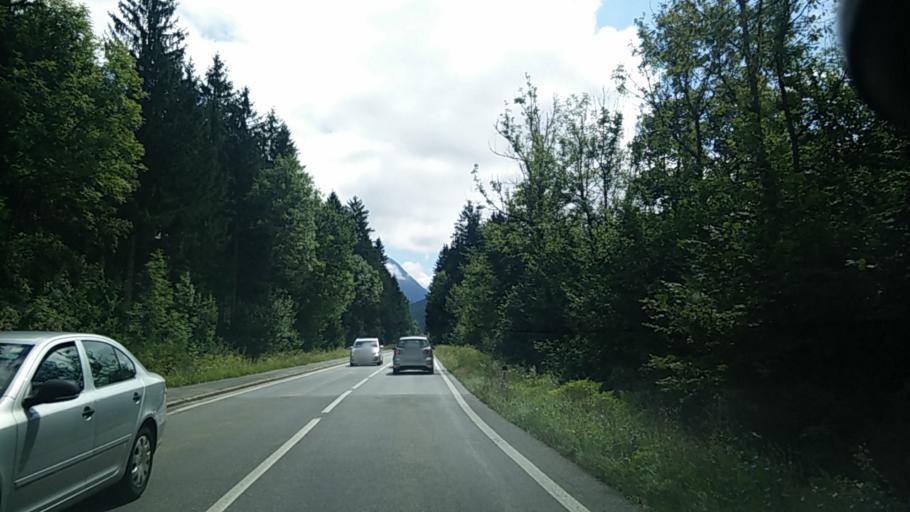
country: AT
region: Carinthia
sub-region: Politischer Bezirk Klagenfurt Land
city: Ferlach
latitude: 46.5326
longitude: 14.2833
